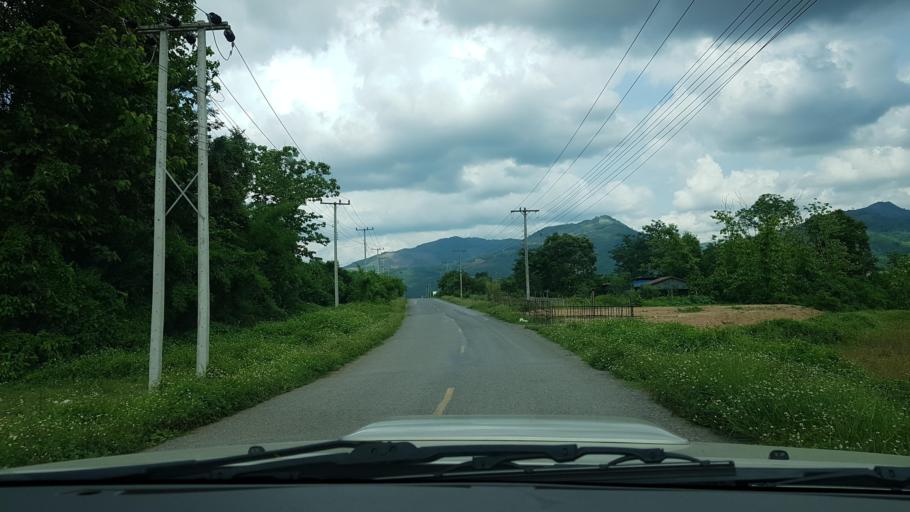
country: LA
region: Loungnamtha
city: Muang Nale
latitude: 20.1517
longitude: 101.4810
